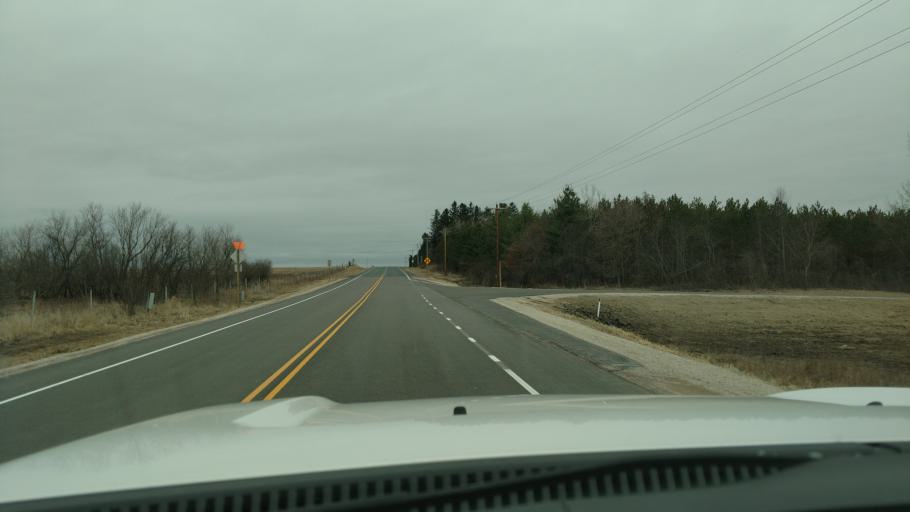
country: US
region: Wisconsin
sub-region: Saint Croix County
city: Hammond
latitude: 44.9388
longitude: -92.4356
